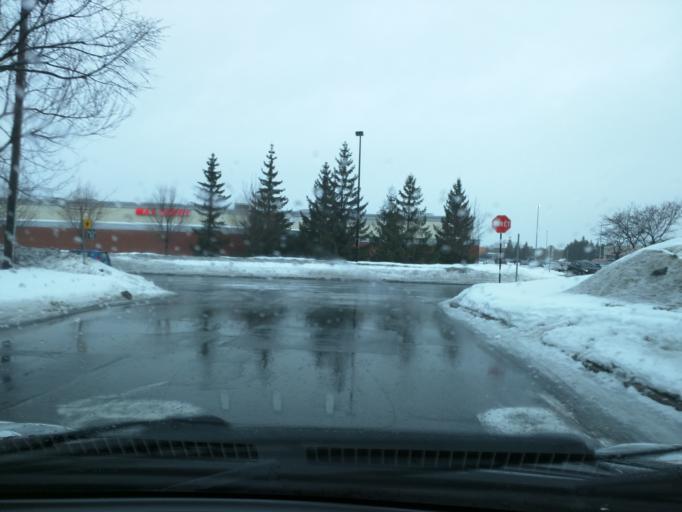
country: CA
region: Quebec
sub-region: Monteregie
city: Longueuil
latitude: 45.5381
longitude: -73.4683
